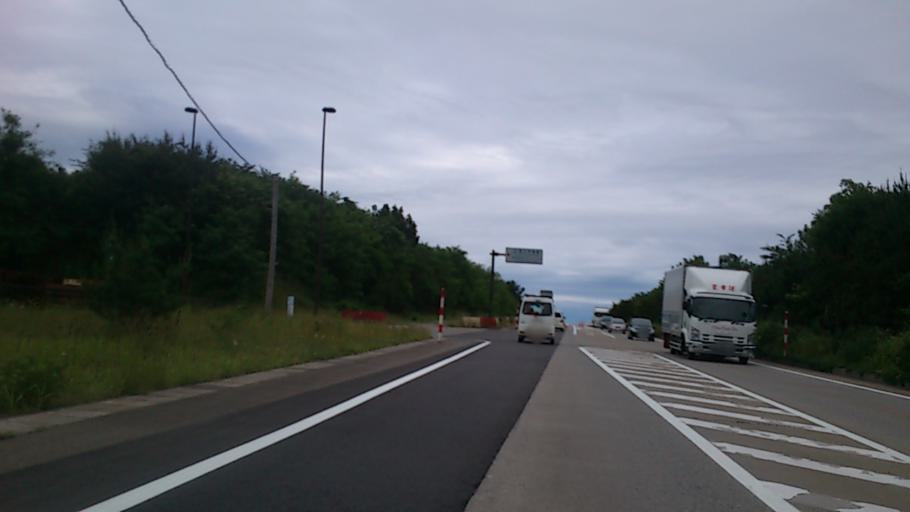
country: JP
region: Akita
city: Akita Shi
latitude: 39.7094
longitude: 140.0740
